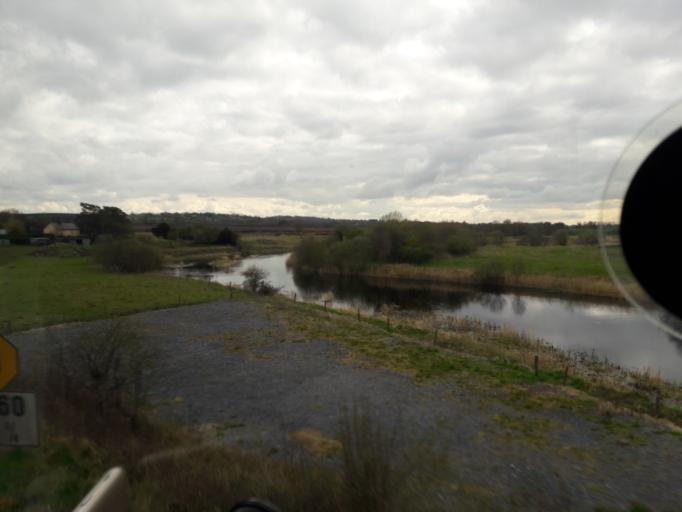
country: IE
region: Leinster
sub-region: An Longfort
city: Granard
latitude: 53.6528
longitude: -7.4343
